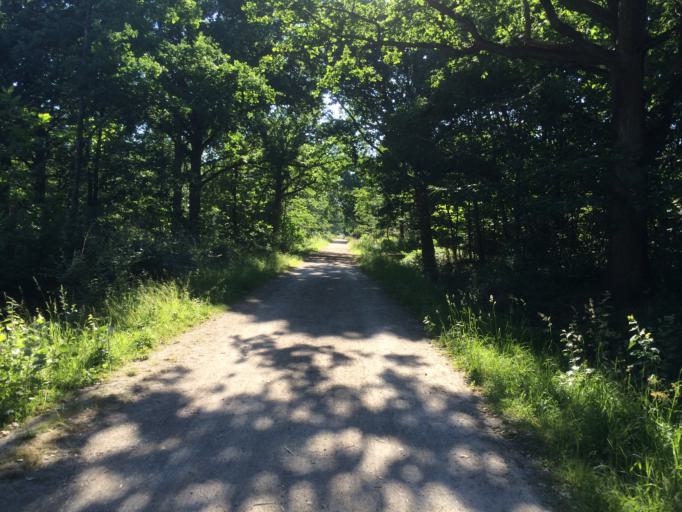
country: FR
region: Ile-de-France
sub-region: Departement du Val-de-Marne
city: Sucy-en-Brie
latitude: 48.7536
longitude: 2.5511
